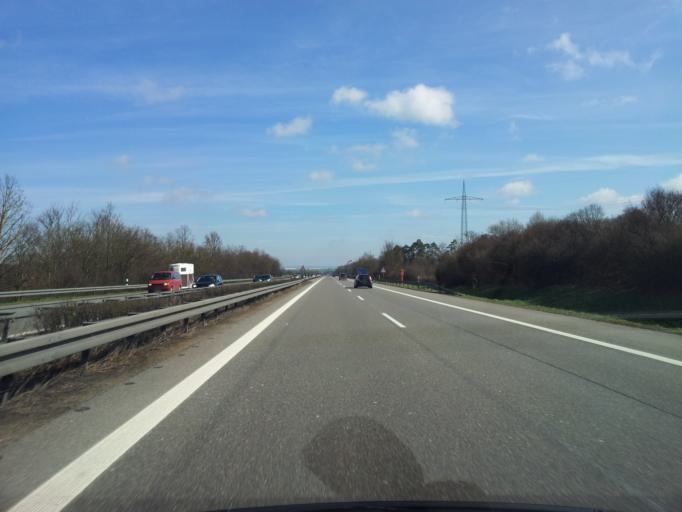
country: DE
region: Baden-Wuerttemberg
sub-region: Karlsruhe Region
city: Horb am Neckar
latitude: 48.4433
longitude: 8.7589
